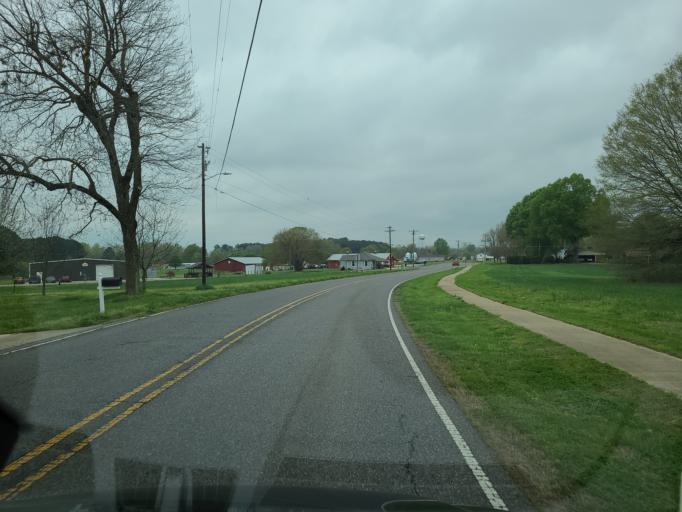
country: US
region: North Carolina
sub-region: Gaston County
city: Cherryville
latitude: 35.4244
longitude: -81.4921
